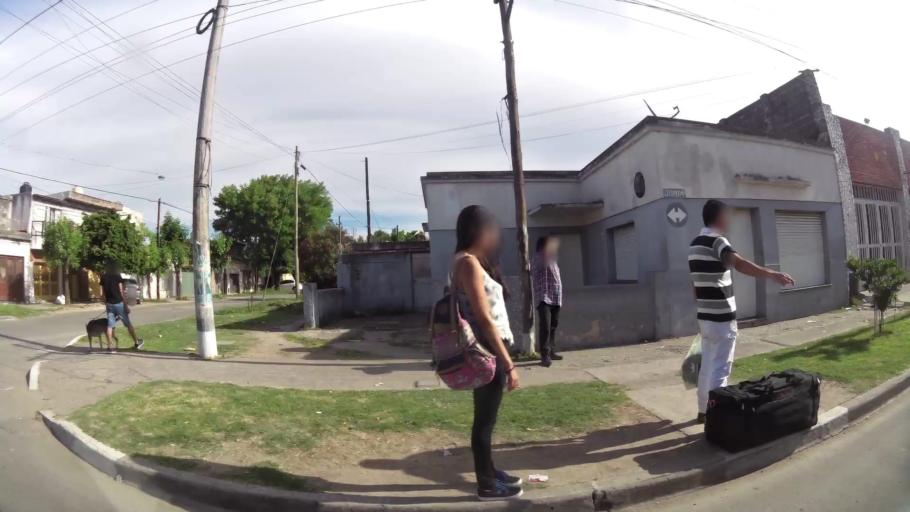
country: AR
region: Santa Fe
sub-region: Departamento de Rosario
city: Rosario
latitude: -32.9273
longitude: -60.6978
